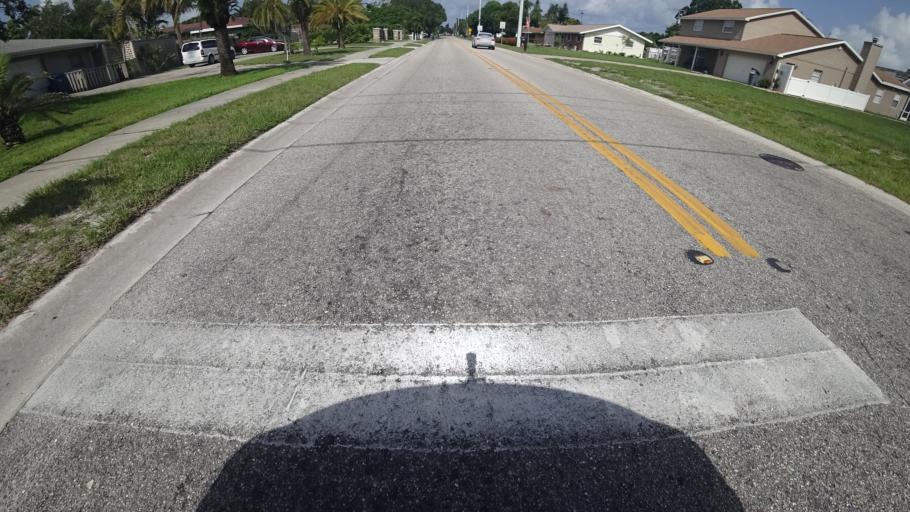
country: US
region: Florida
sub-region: Manatee County
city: West Bradenton
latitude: 27.5144
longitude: -82.6366
